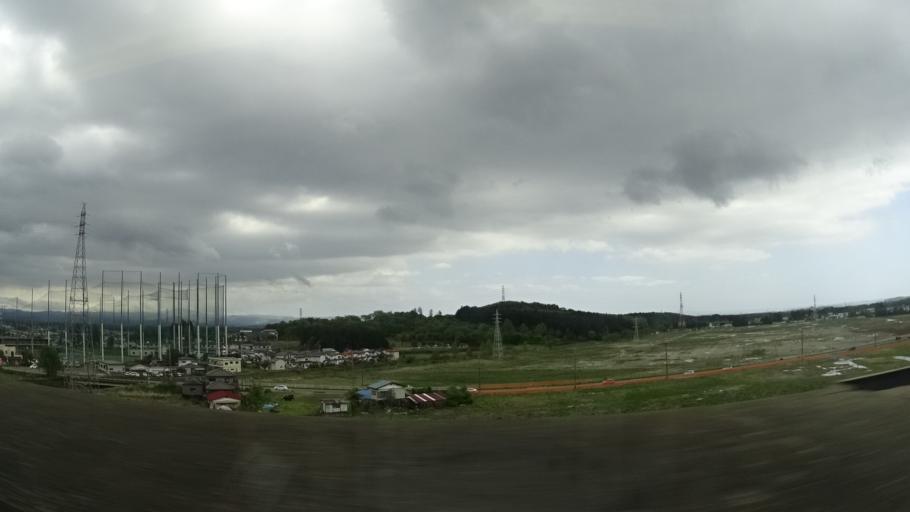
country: JP
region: Tochigi
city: Kuroiso
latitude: 36.9230
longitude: 140.0139
